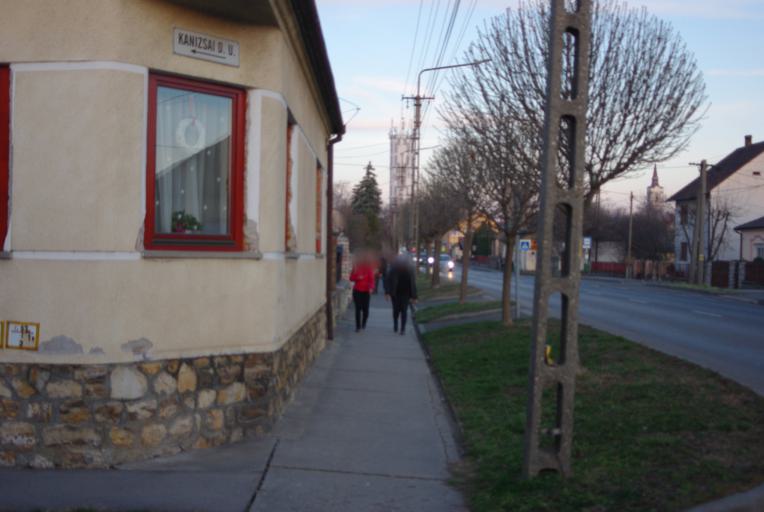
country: HU
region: Baranya
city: Mohacs
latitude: 45.9963
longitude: 18.6759
